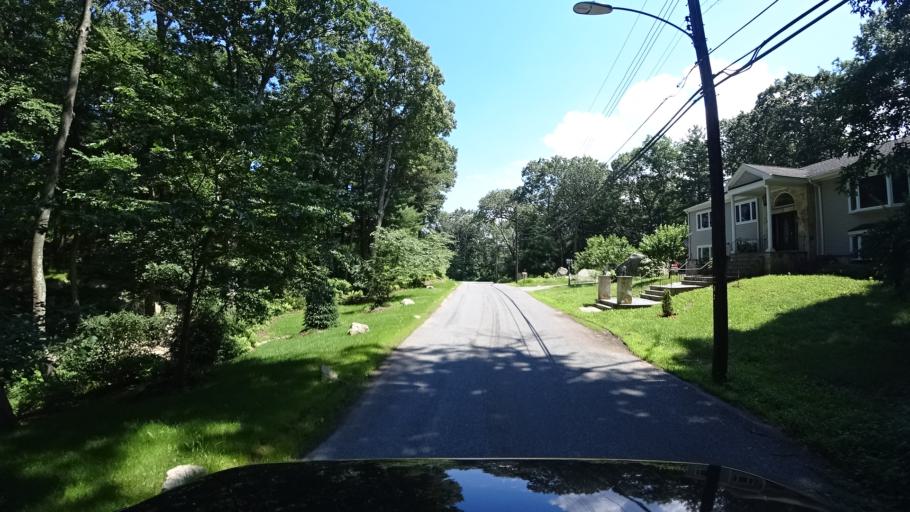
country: US
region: Massachusetts
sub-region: Norfolk County
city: Dedham
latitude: 42.2412
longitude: -71.1861
